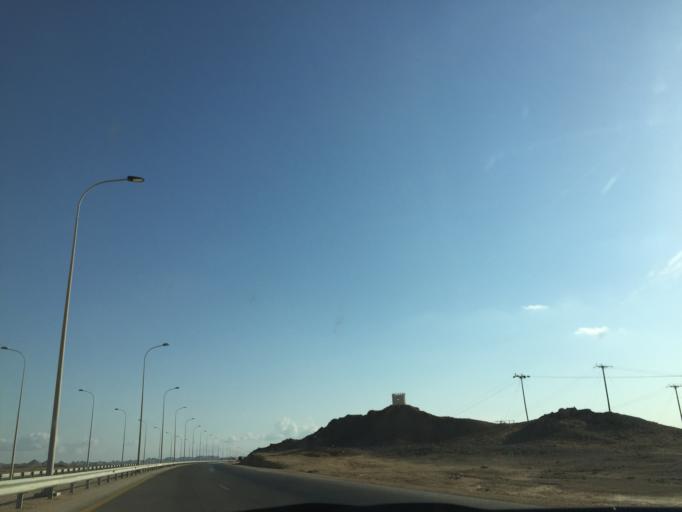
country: OM
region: Zufar
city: Salalah
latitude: 17.5374
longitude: 54.0550
